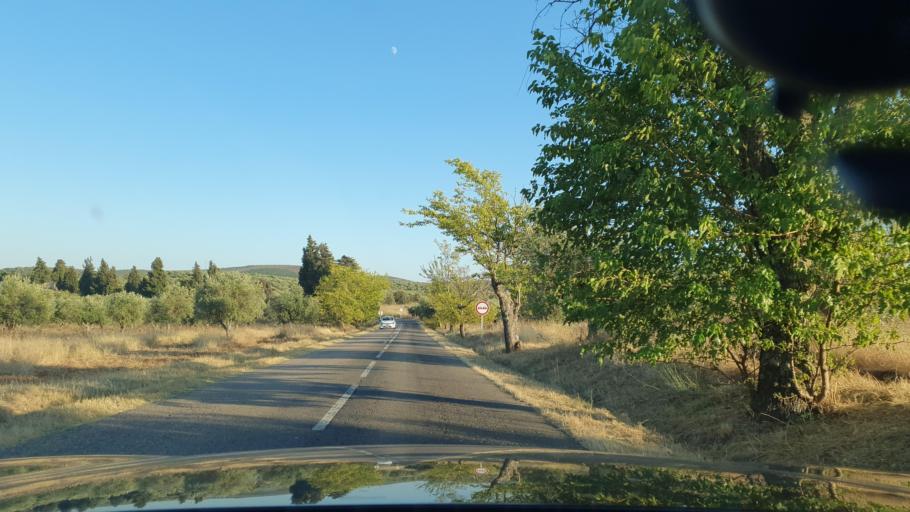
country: PT
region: Portalegre
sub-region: Fronteira
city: Fronteira
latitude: 38.9405
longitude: -7.6762
